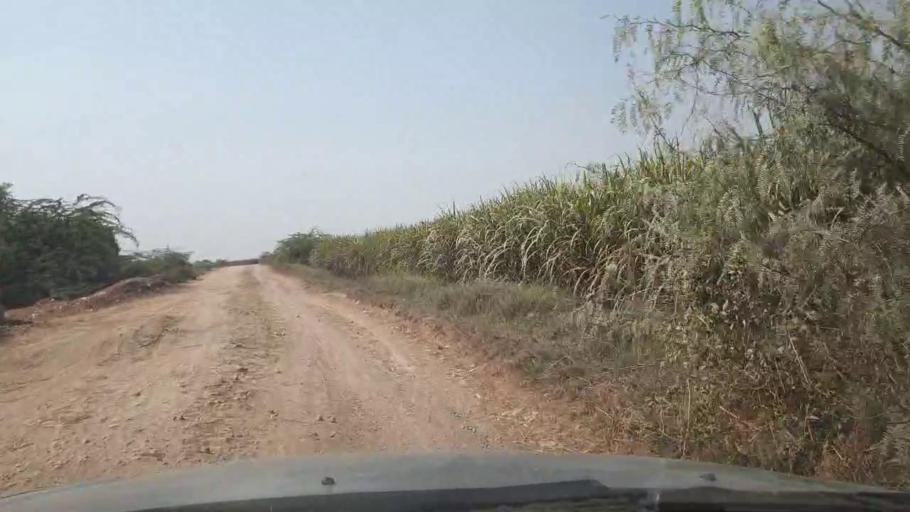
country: PK
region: Sindh
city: Bulri
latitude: 24.8675
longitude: 68.3278
